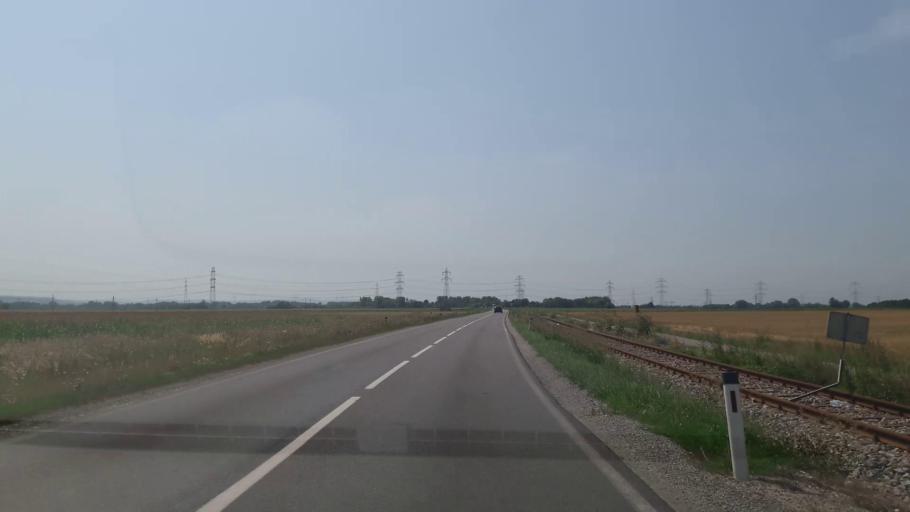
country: AT
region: Lower Austria
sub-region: Politischer Bezirk Bruck an der Leitha
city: Gotzendorf an der Leitha
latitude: 48.0369
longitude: 16.6015
